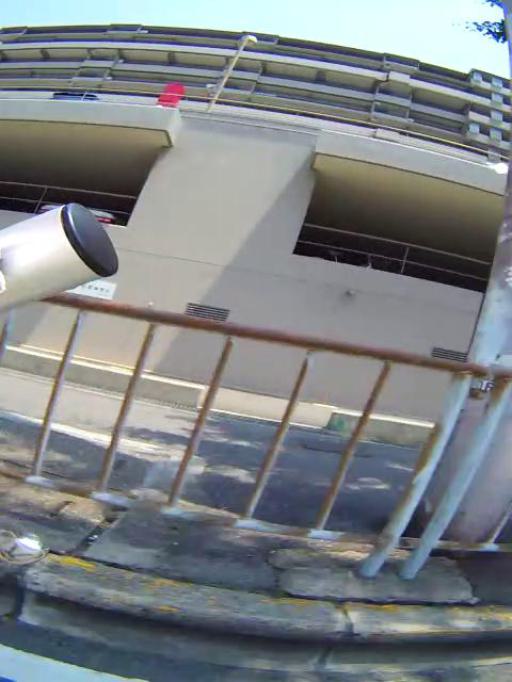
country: JP
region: Osaka
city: Toyonaka
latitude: 34.7839
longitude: 135.4974
